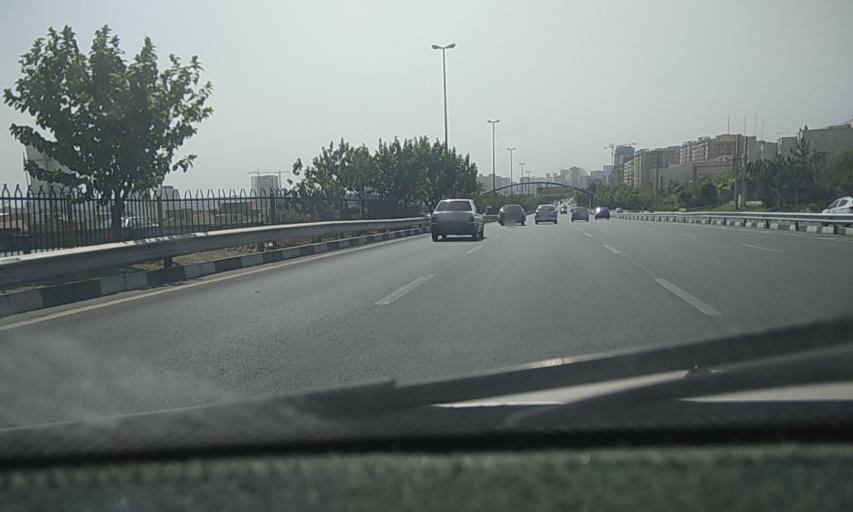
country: IR
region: Tehran
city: Shahr-e Qods
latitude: 35.7592
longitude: 51.2394
